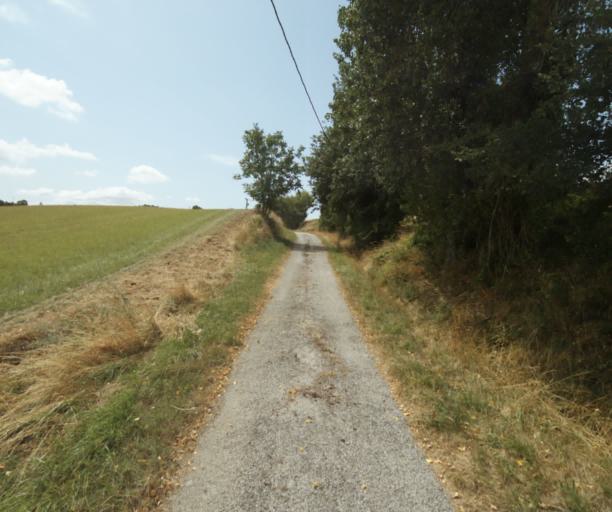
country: FR
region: Midi-Pyrenees
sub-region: Departement de la Haute-Garonne
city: Saint-Felix-Lauragais
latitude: 43.4460
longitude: 1.8918
